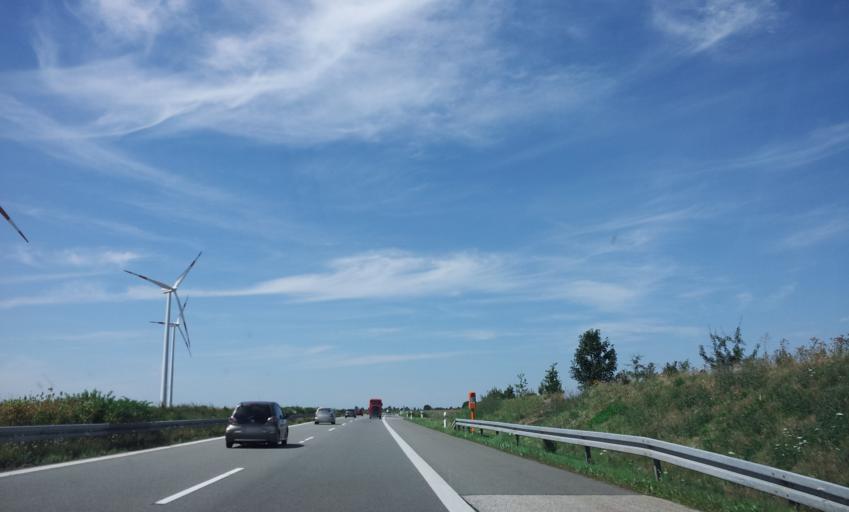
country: DE
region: Mecklenburg-Vorpommern
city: Gormin
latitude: 53.9971
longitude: 13.3190
